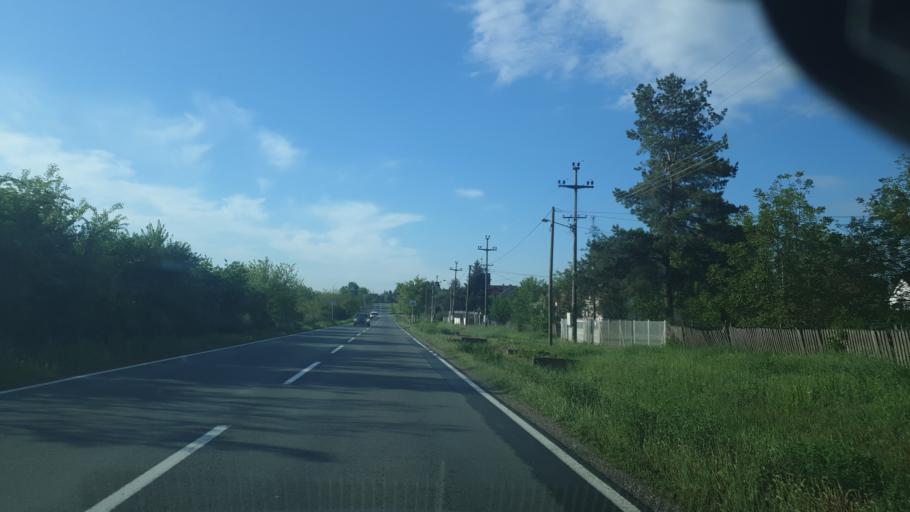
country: RS
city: Stubline
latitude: 44.5831
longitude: 20.1511
